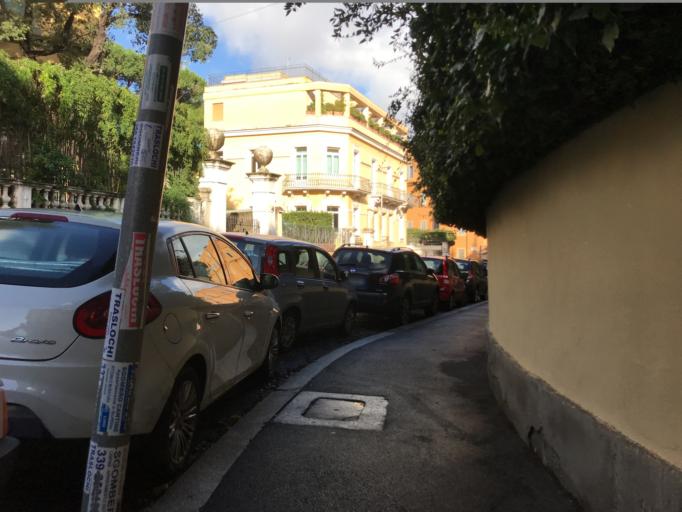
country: IT
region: Latium
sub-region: Citta metropolitana di Roma Capitale
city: Rome
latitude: 41.9108
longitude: 12.5065
